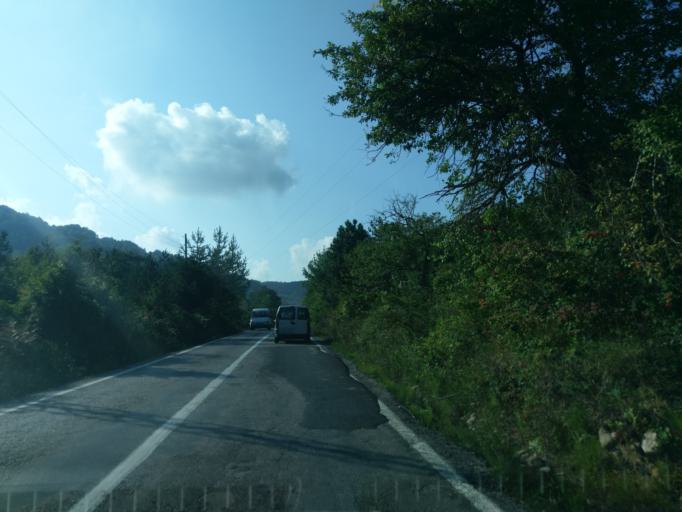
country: TR
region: Sinop
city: Ayancik
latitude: 41.8797
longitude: 34.5273
